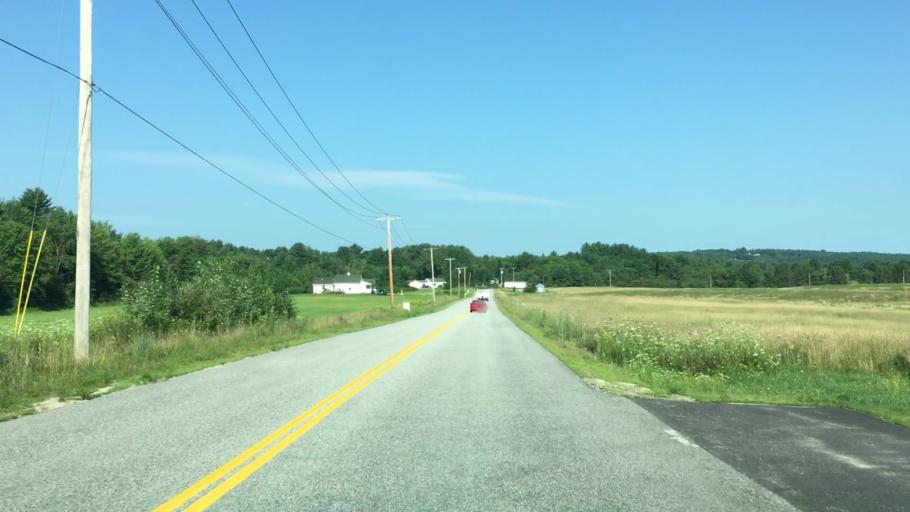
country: US
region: Maine
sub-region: Androscoggin County
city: Minot
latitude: 44.0436
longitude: -70.3242
